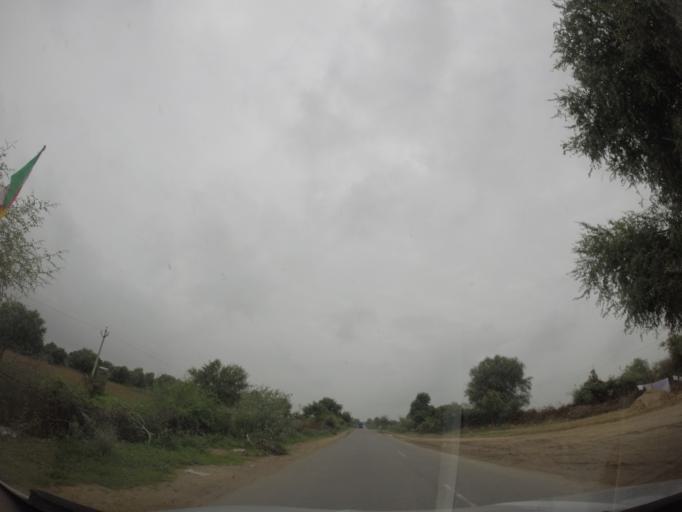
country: IN
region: Rajasthan
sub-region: Jalore
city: Sanchor
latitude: 24.6742
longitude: 71.8391
